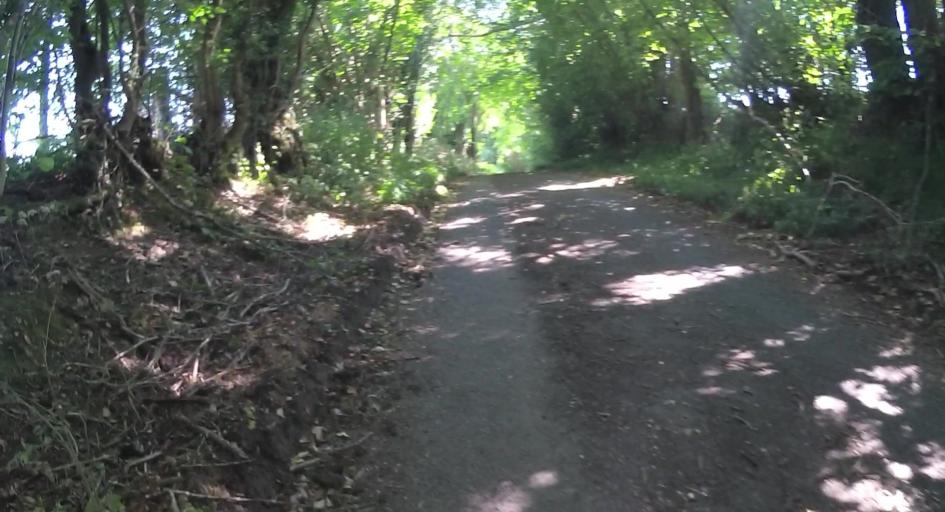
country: GB
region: England
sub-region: Hampshire
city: Kingsclere
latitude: 51.3537
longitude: -1.2743
